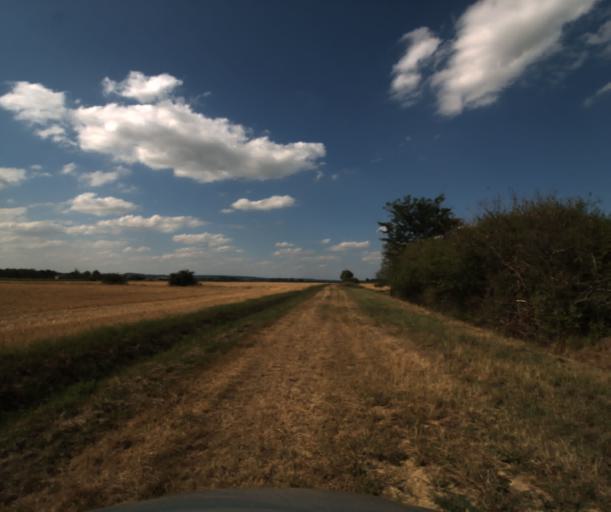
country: FR
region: Midi-Pyrenees
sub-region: Departement de la Haute-Garonne
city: Saint-Lys
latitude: 43.5198
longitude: 1.1771
